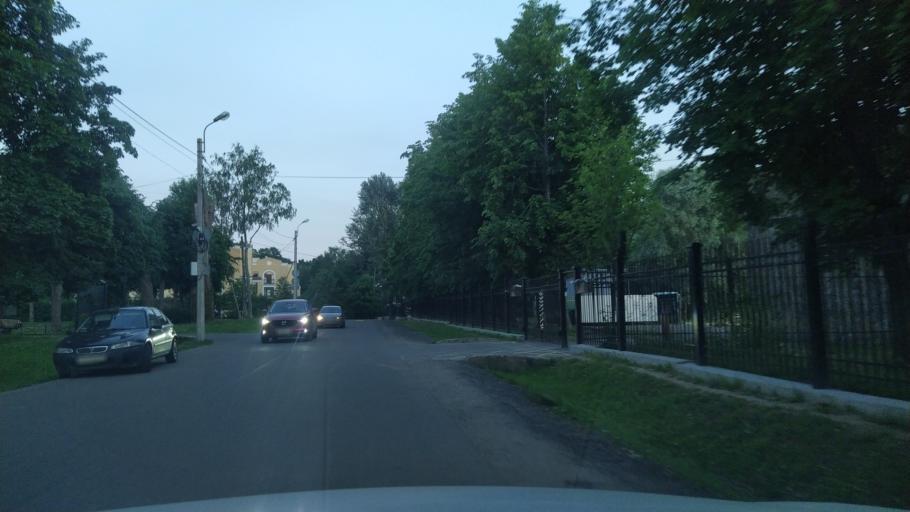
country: RU
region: St.-Petersburg
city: Sestroretsk
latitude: 60.0909
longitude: 29.9423
